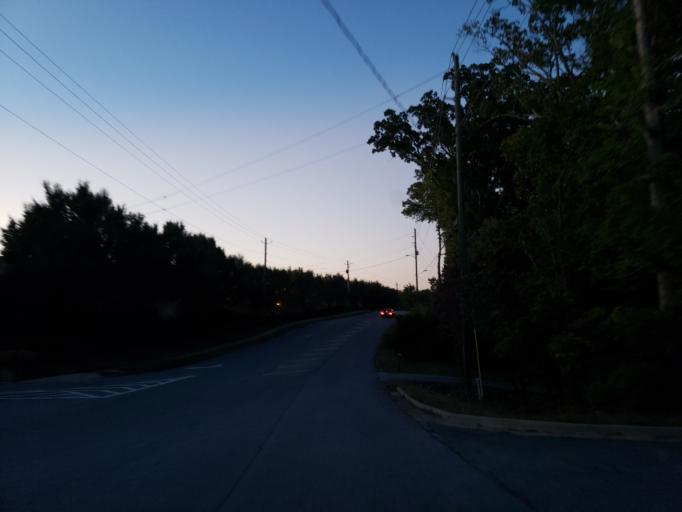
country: US
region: Georgia
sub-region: Cobb County
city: Fair Oaks
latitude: 33.9143
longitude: -84.5572
